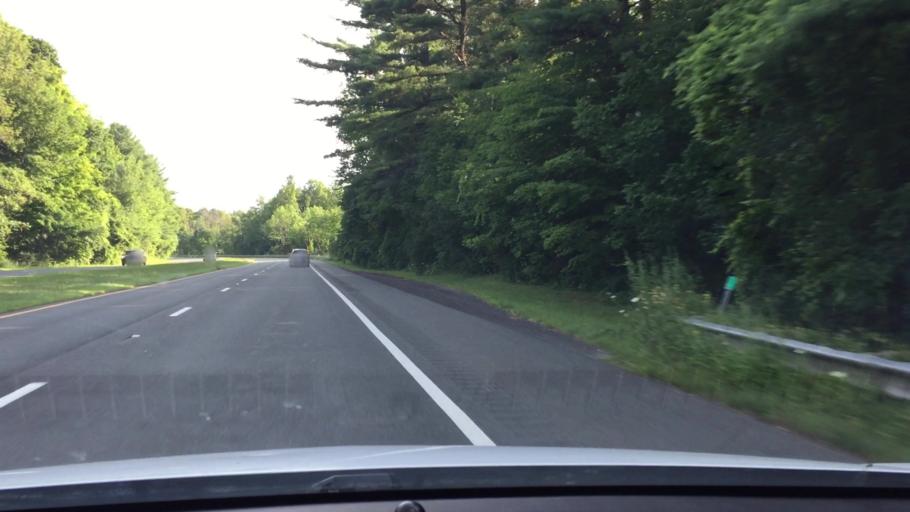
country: US
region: Massachusetts
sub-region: Berkshire County
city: Lenox
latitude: 42.3497
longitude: -73.2684
